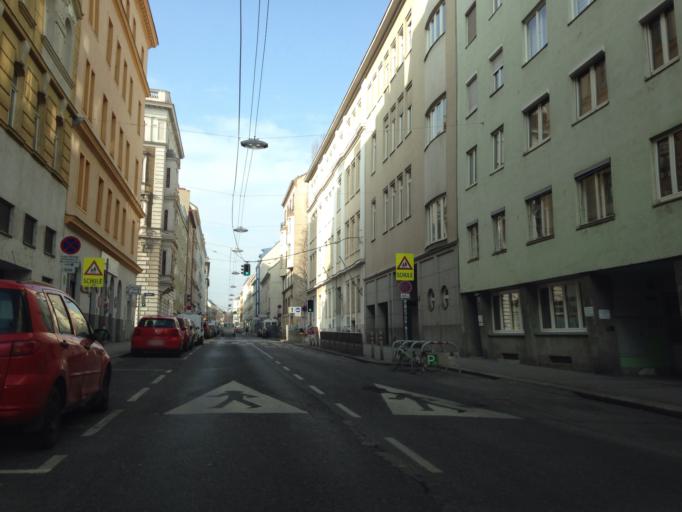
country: AT
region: Vienna
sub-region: Wien Stadt
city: Vienna
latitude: 48.2059
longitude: 16.3421
